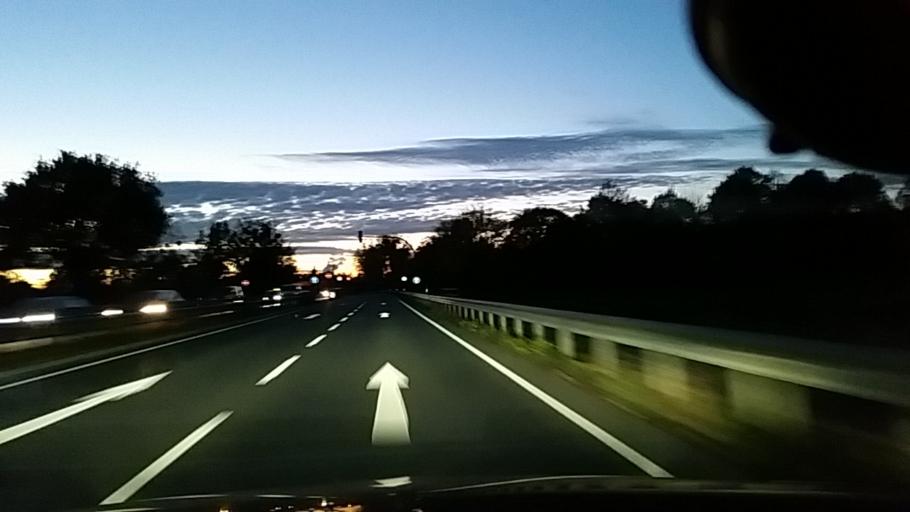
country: DE
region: Lower Saxony
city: Wolfsburg
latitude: 52.4402
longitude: 10.8187
